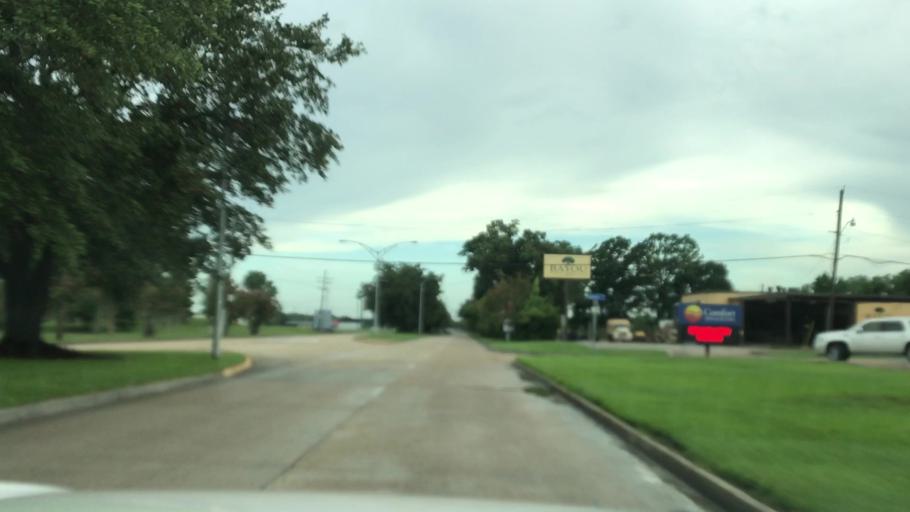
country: US
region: Louisiana
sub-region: East Baton Rouge Parish
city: Brownsfield
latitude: 30.5300
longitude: -91.1613
